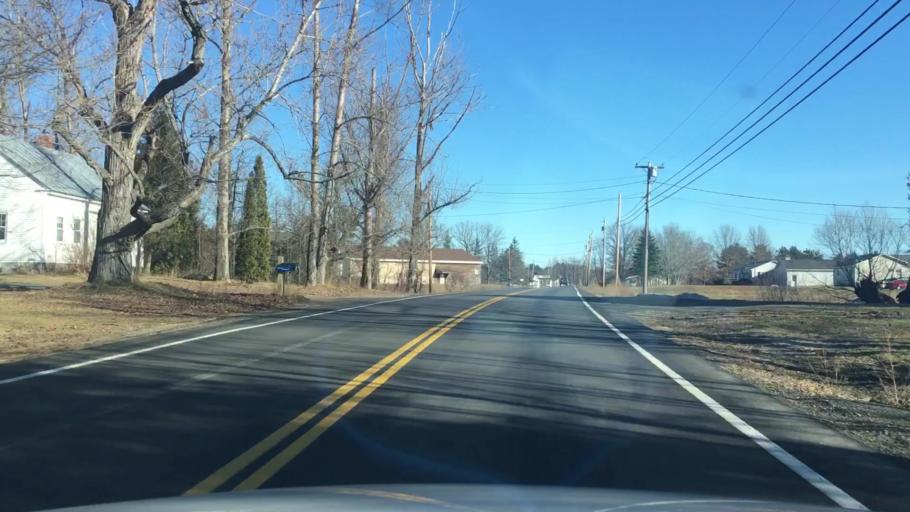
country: US
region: Maine
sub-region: Kennebec County
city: Benton
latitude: 44.6034
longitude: -69.5381
